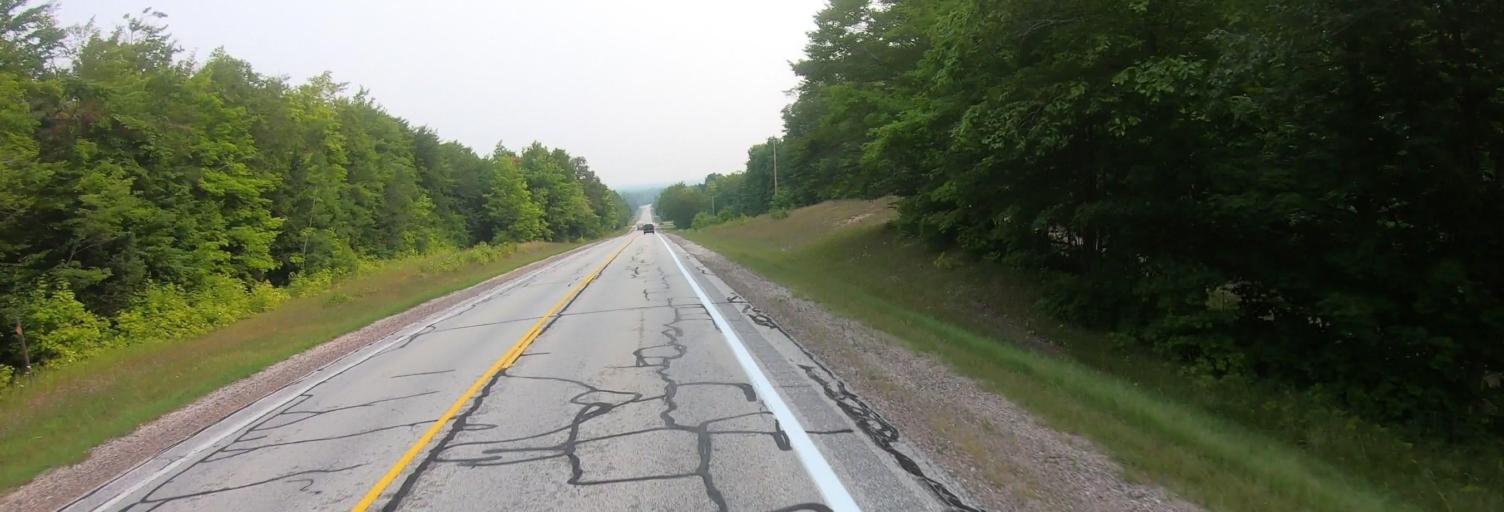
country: US
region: Michigan
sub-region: Luce County
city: Newberry
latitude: 46.4983
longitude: -85.0956
